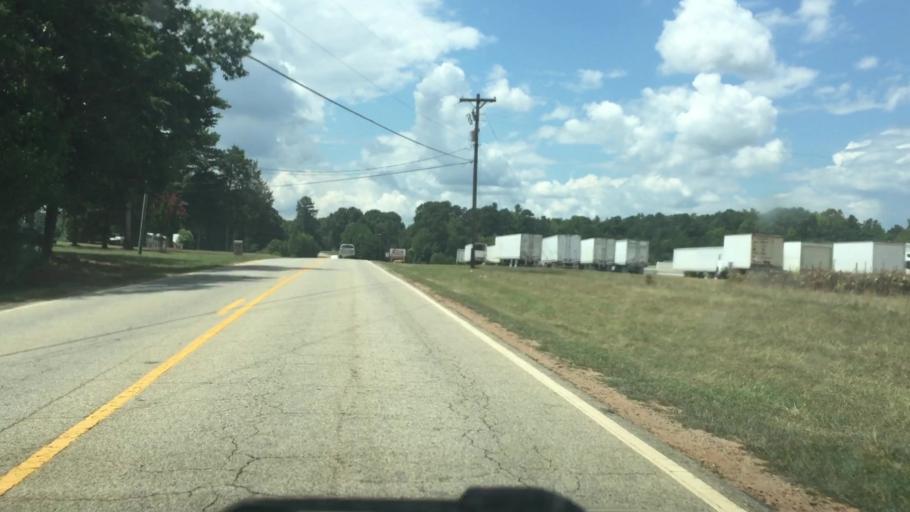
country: US
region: North Carolina
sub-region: Rowan County
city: Landis
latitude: 35.6176
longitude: -80.6515
